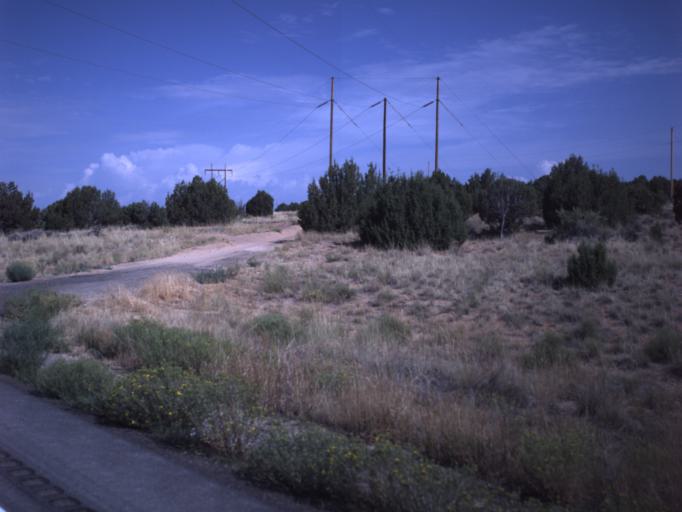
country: US
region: Utah
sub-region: Uintah County
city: Naples
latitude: 40.3220
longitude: -109.2596
